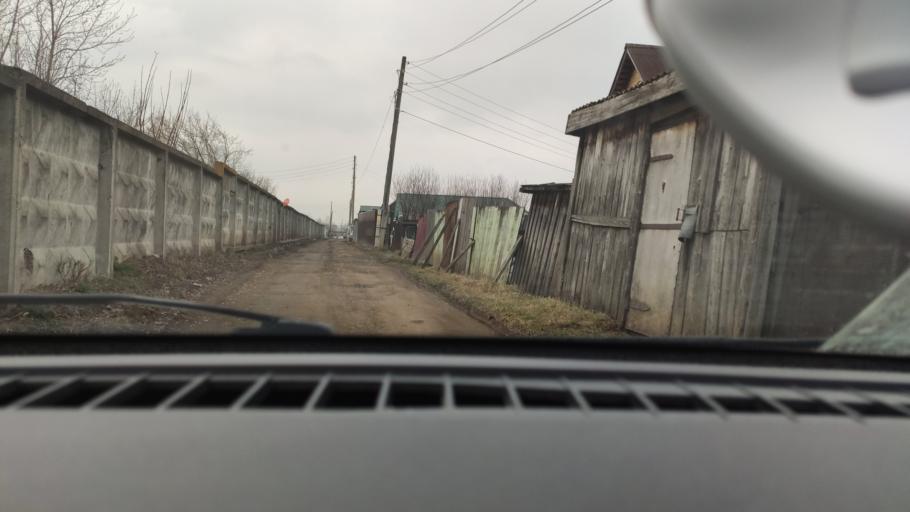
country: RU
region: Perm
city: Kondratovo
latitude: 57.9868
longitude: 56.1119
